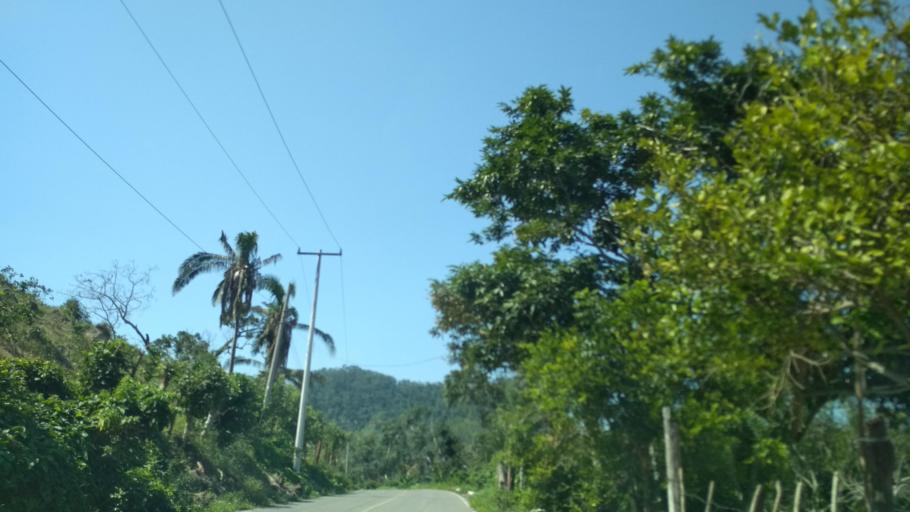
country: MX
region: Veracruz
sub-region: Papantla
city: Polutla
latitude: 20.4743
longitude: -97.2148
